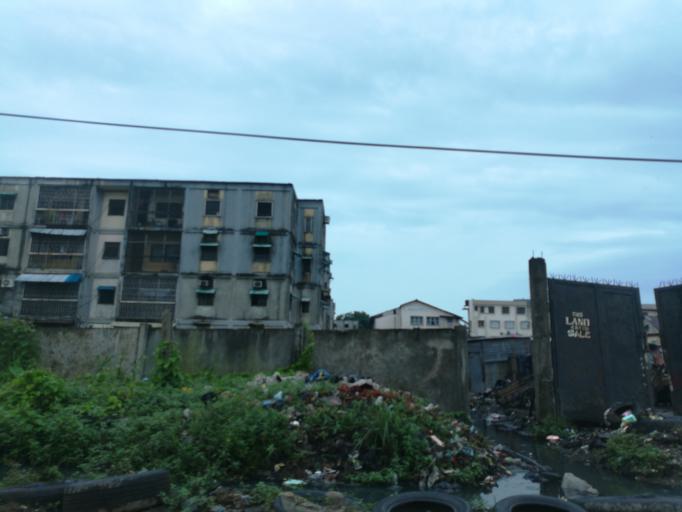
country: NG
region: Lagos
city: Makoko
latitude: 6.4914
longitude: 3.3839
